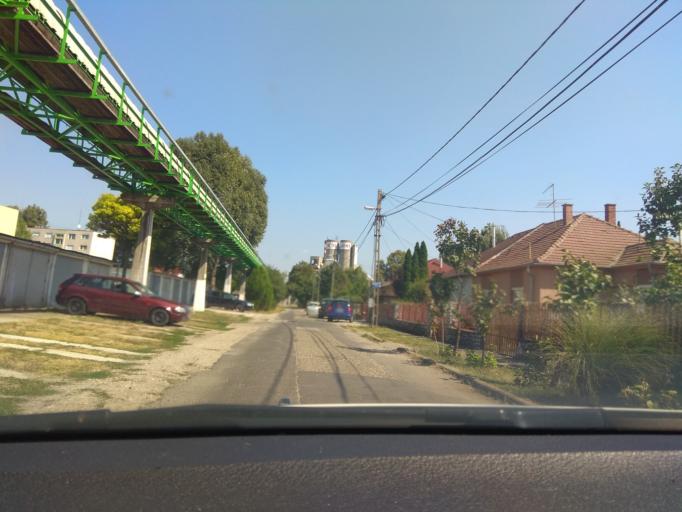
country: HU
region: Borsod-Abauj-Zemplen
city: Miskolc
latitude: 48.0654
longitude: 20.7876
